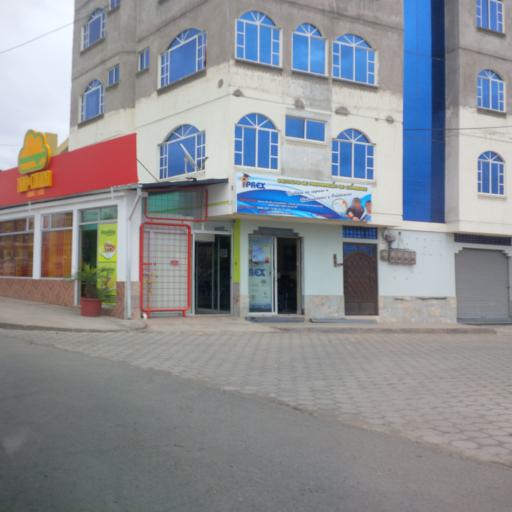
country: EC
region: Chimborazo
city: Riobamba
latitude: -1.6535
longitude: -78.6737
